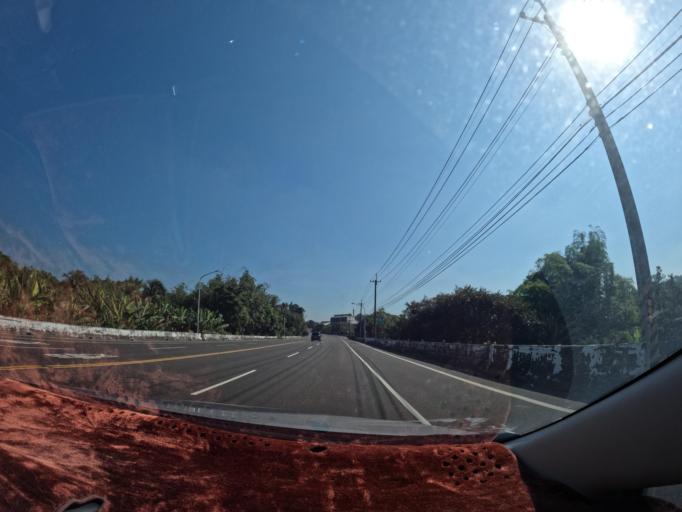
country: TW
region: Taiwan
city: Yujing
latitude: 23.0601
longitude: 120.3929
